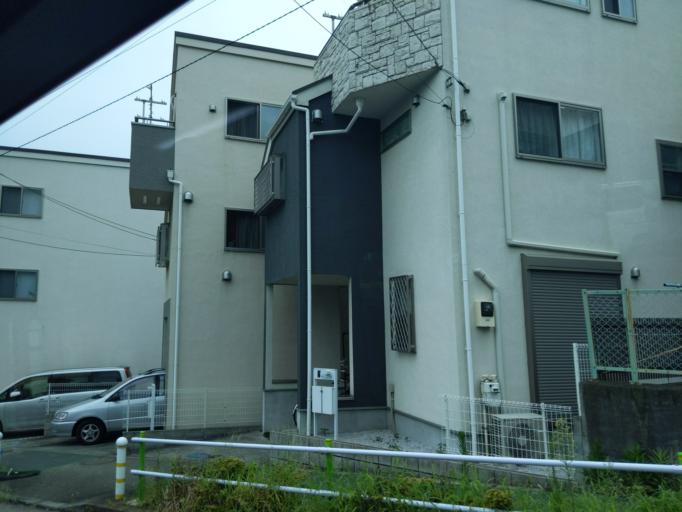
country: JP
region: Saitama
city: Wako
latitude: 35.7757
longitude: 139.6554
